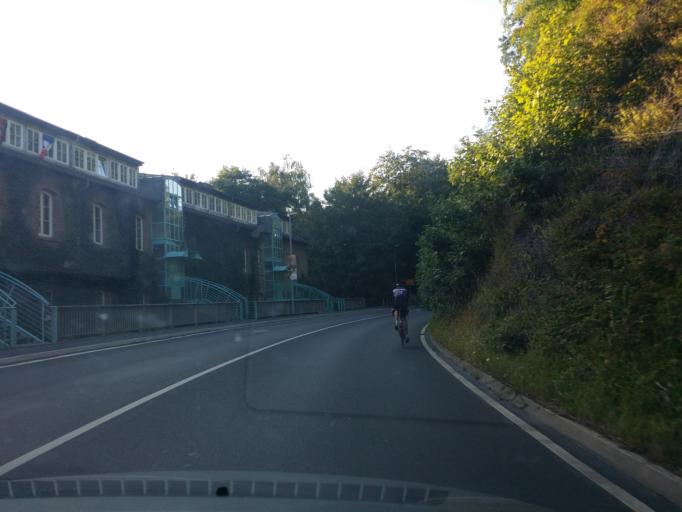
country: DE
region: Hesse
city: Eppstein
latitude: 50.1200
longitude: 8.4170
